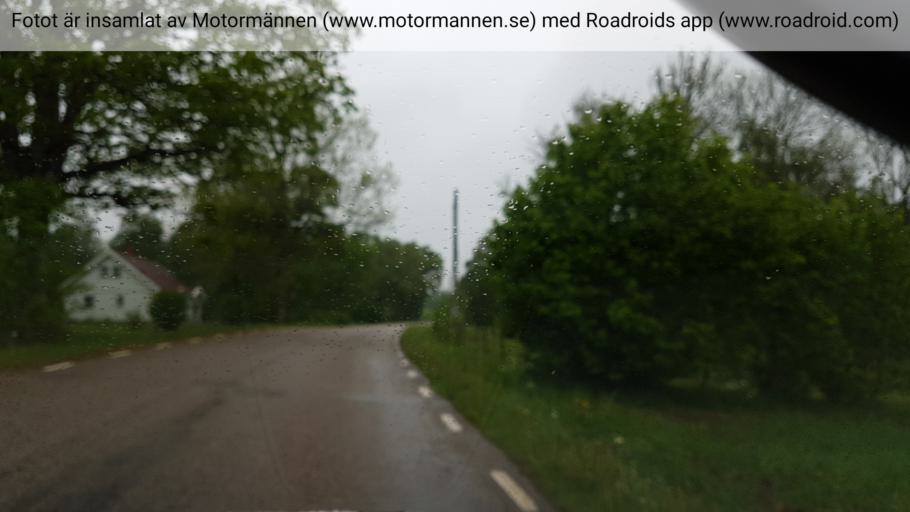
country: SE
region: Vaestra Goetaland
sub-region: Ulricehamns Kommun
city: Ulricehamn
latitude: 57.8009
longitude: 13.5794
